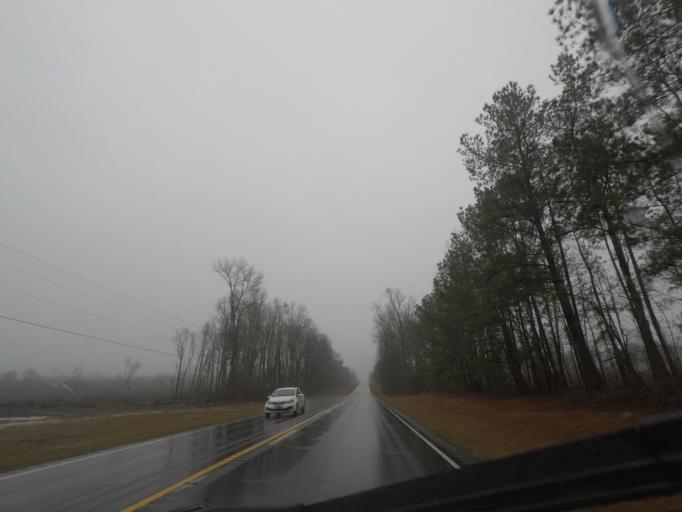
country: US
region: North Carolina
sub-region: Scotland County
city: Laurinburg
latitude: 34.8282
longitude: -79.4591
